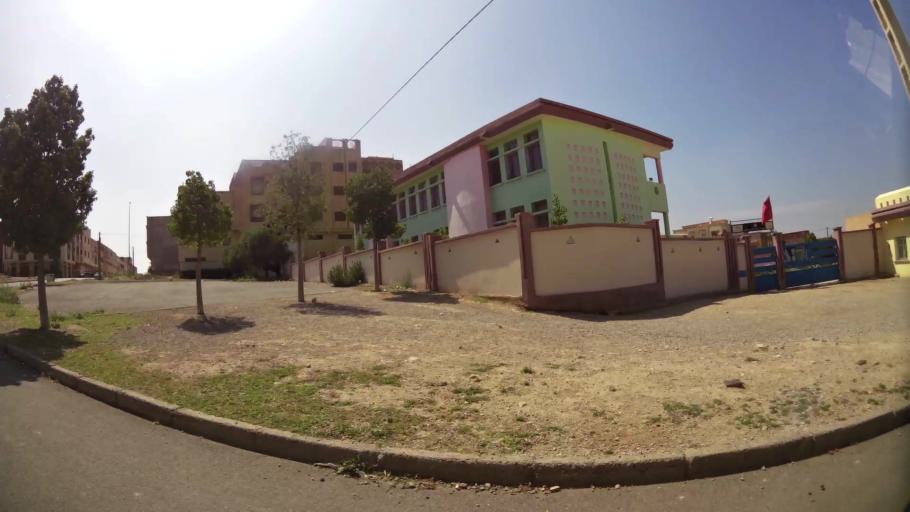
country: MA
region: Oriental
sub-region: Oujda-Angad
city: Oujda
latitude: 34.6896
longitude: -1.8700
